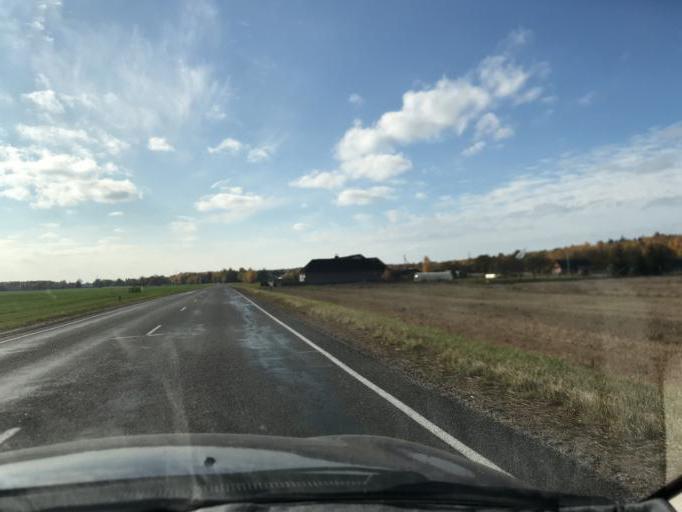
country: BY
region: Grodnenskaya
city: Voranava
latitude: 54.1888
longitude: 25.3419
